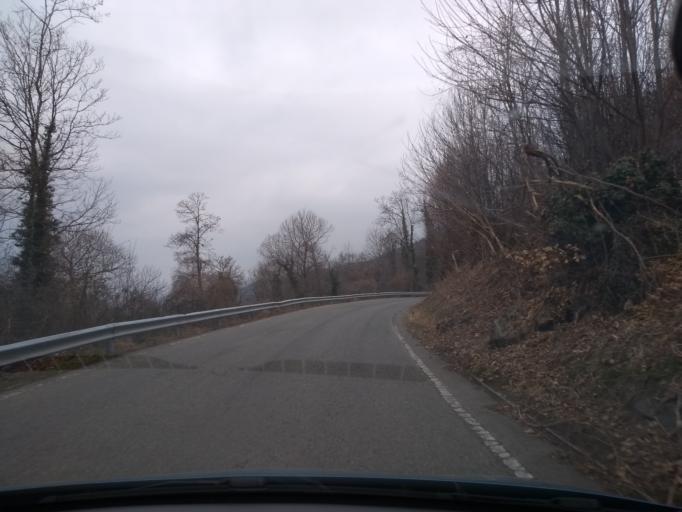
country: IT
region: Piedmont
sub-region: Provincia di Torino
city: Palazzo Canavese
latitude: 45.4719
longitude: 7.9675
